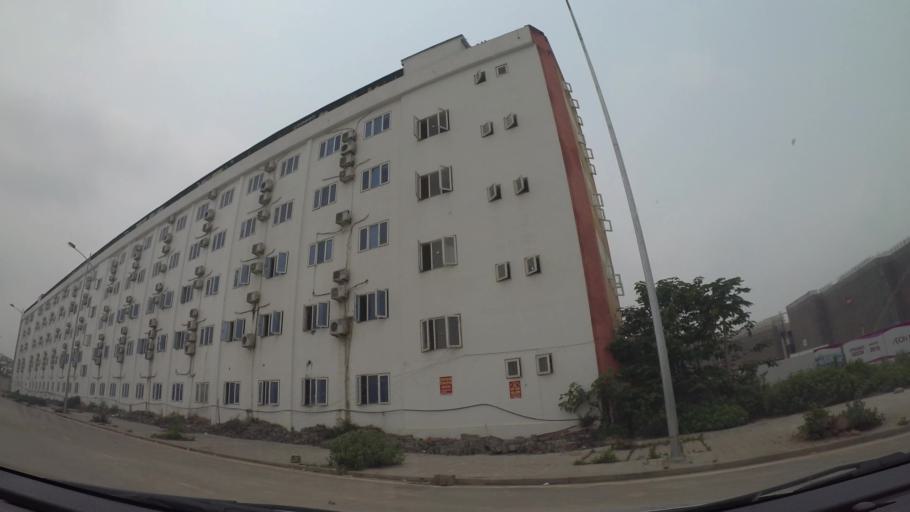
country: VN
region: Ha Noi
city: Ha Dong
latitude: 20.9894
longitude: 105.7530
